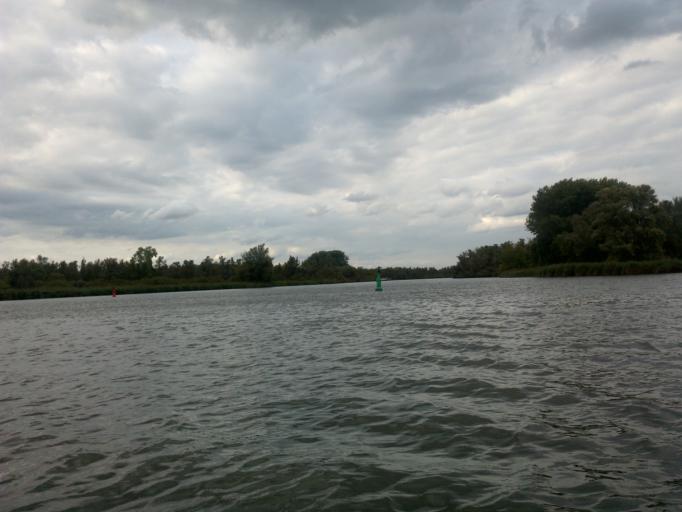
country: NL
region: North Brabant
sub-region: Gemeente Geertruidenberg
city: Geertruidenberg
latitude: 51.7264
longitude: 4.8477
